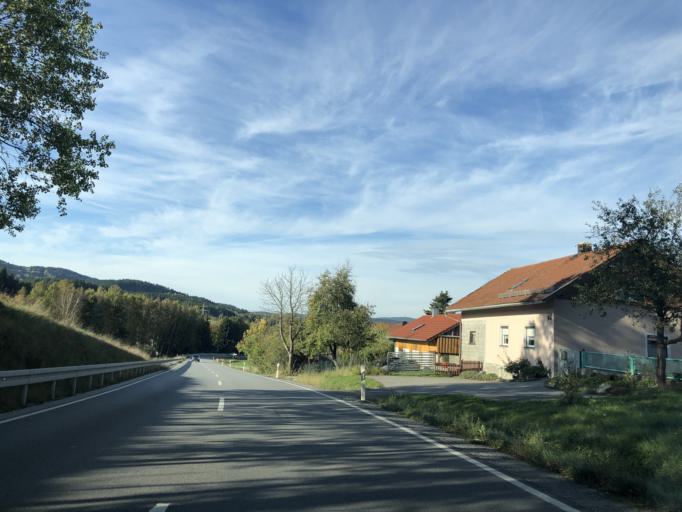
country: DE
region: Bavaria
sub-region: Lower Bavaria
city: Ruhmannsfelden
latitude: 48.9969
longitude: 12.9817
